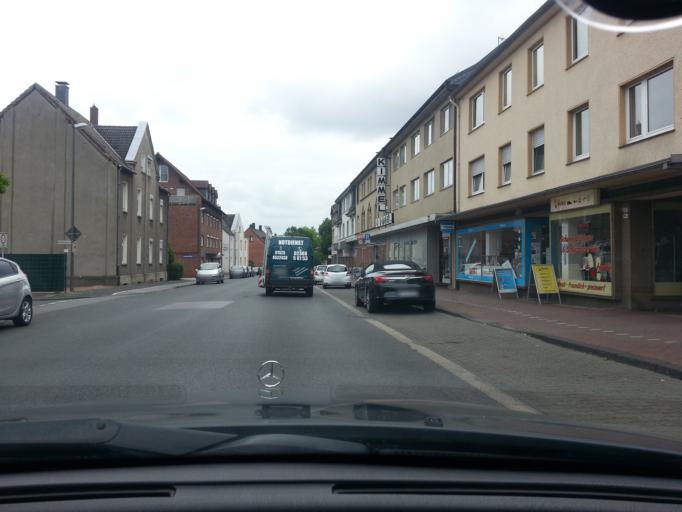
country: DE
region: North Rhine-Westphalia
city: Oer-Erkenschwick
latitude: 51.6449
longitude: 7.2564
